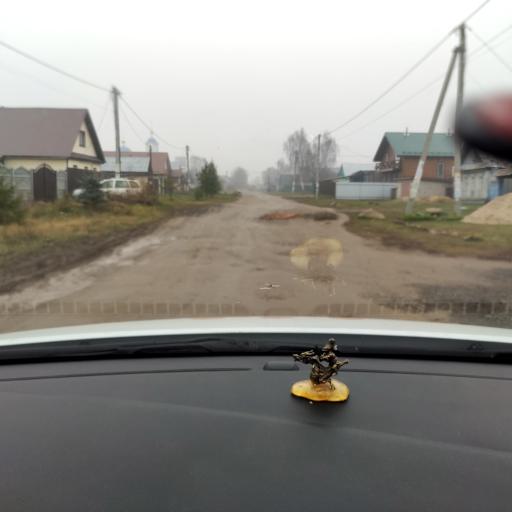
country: RU
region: Tatarstan
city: Osinovo
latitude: 55.8833
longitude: 48.8813
